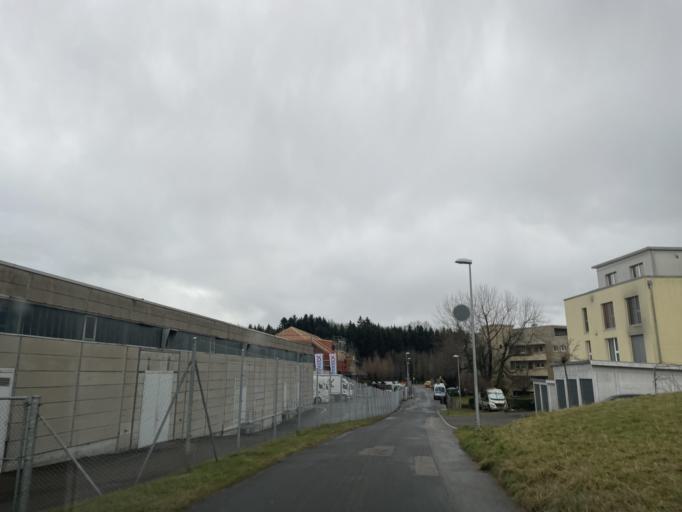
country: CH
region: Bern
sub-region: Bern-Mittelland District
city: Zollikofen
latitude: 47.0126
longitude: 7.4614
